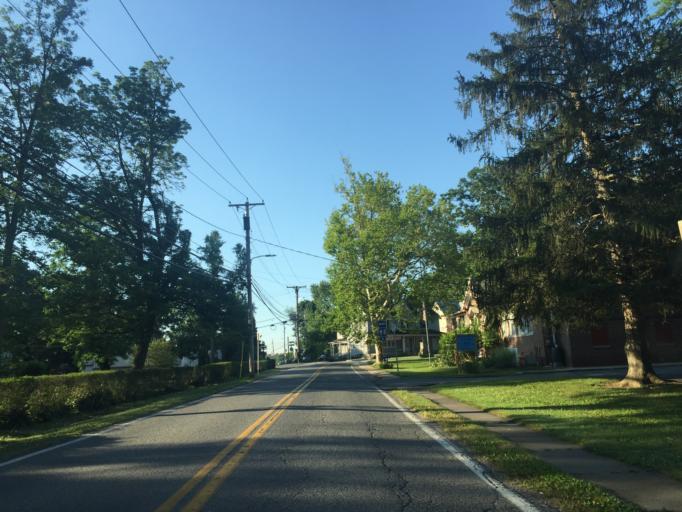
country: US
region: Maryland
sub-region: Howard County
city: Elkridge
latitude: 39.2280
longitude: -76.7067
